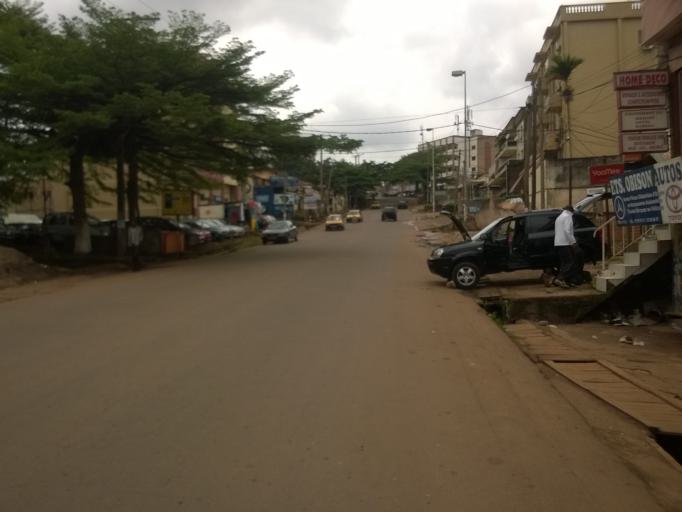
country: CM
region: Centre
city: Yaounde
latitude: 3.8747
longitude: 11.5243
